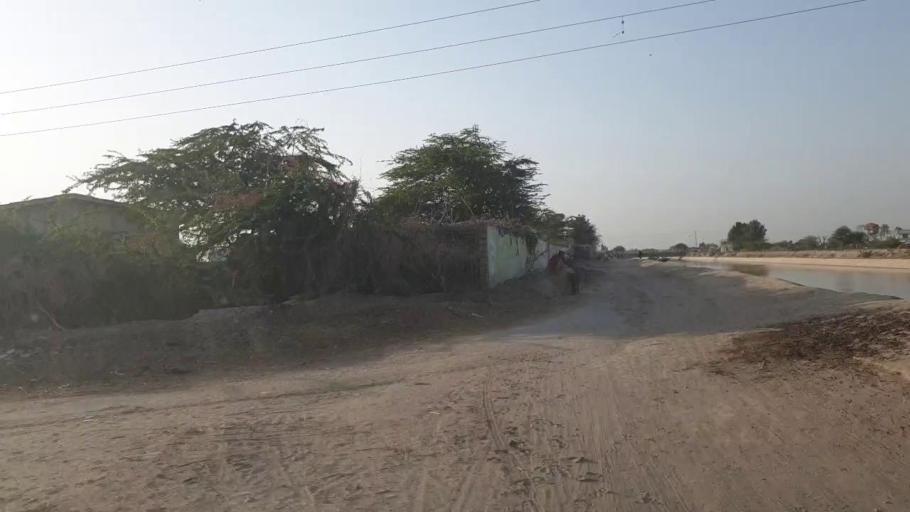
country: PK
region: Sindh
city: Dhoro Naro
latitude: 25.4959
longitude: 69.5617
